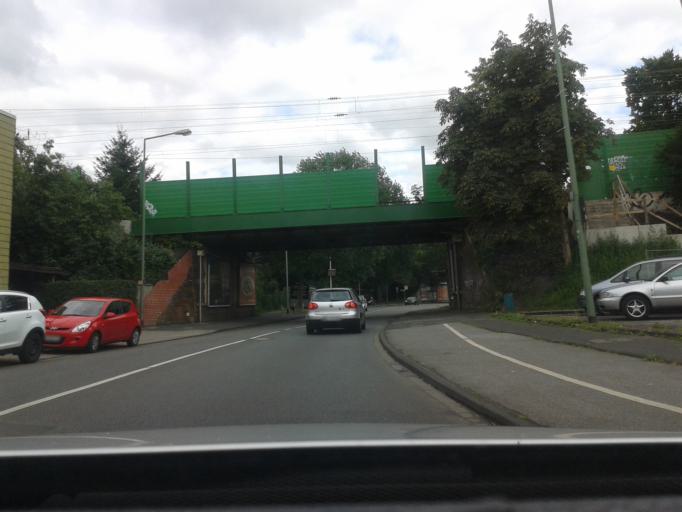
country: DE
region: North Rhine-Westphalia
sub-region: Regierungsbezirk Dusseldorf
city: Duisburg
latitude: 51.4162
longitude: 6.7917
